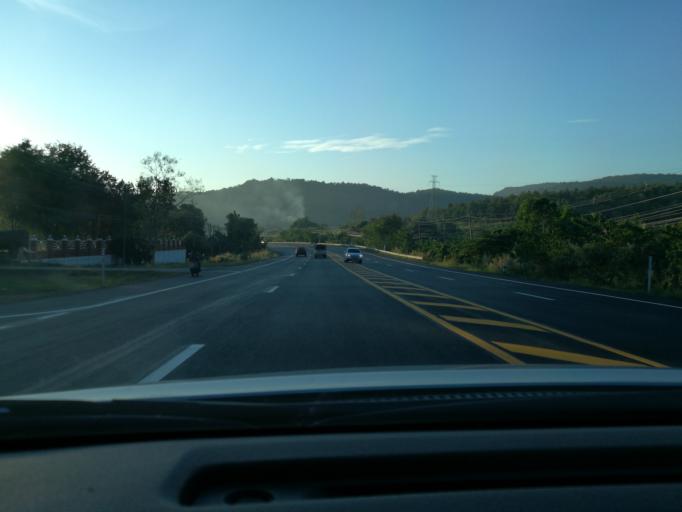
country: TH
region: Phitsanulok
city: Wang Thong
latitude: 16.8660
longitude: 100.4932
